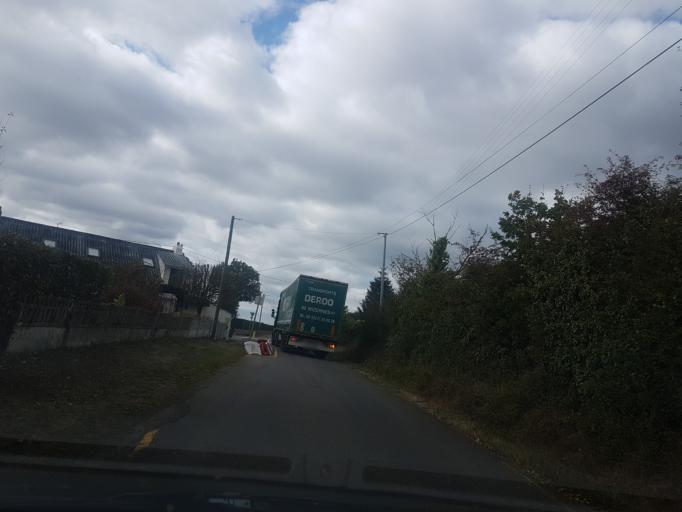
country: FR
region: Pays de la Loire
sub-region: Departement de la Loire-Atlantique
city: Saint-Mars-du-Desert
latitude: 47.3916
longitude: -1.4114
